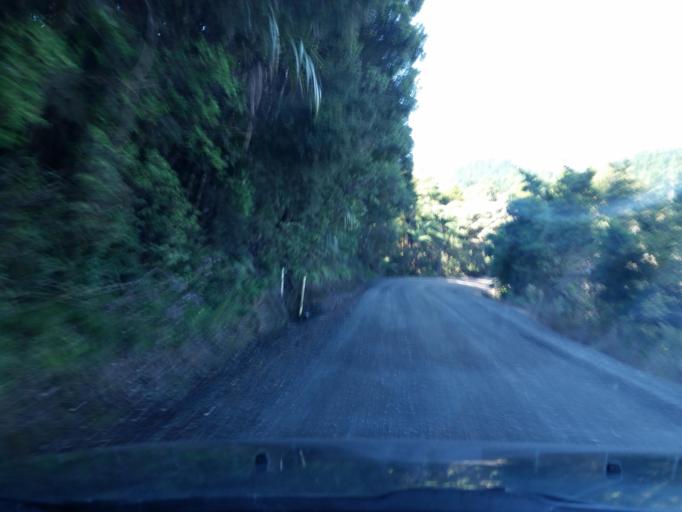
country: NZ
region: Northland
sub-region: Far North District
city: Waimate North
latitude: -35.6094
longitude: 173.7120
